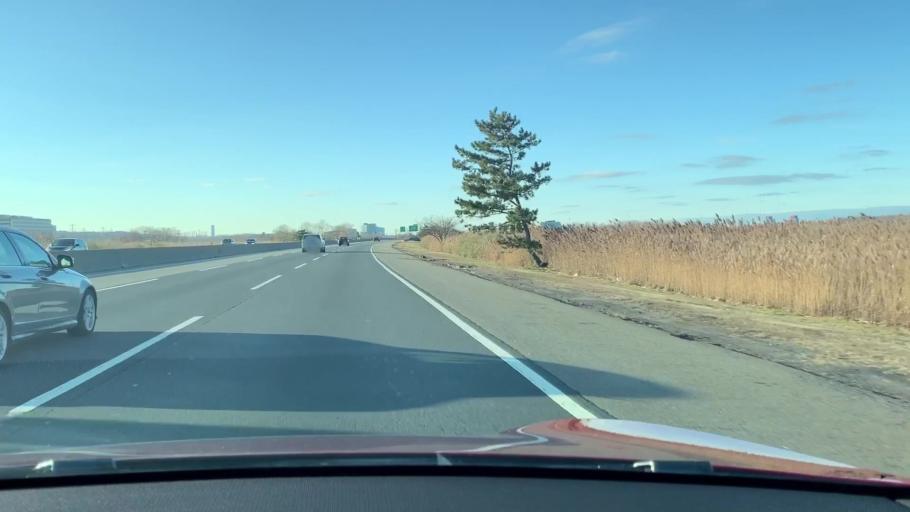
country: US
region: New Jersey
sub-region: Hudson County
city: North Bergen
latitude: 40.8068
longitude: -74.0321
